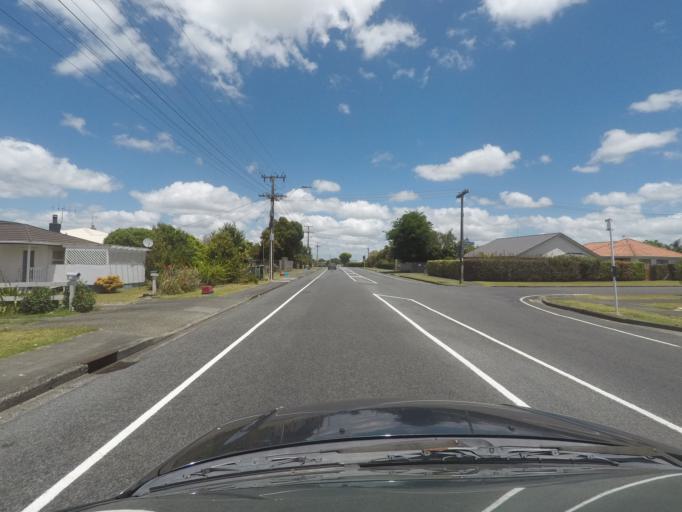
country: NZ
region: Northland
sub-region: Whangarei
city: Whangarei
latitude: -35.7588
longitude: 174.3674
